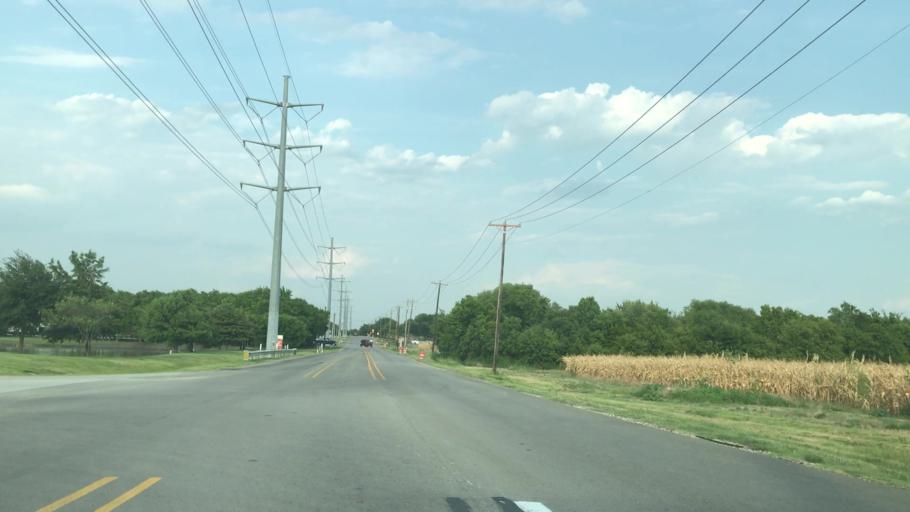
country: US
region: Texas
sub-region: Rockwall County
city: Fate
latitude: 32.9369
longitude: -96.3955
